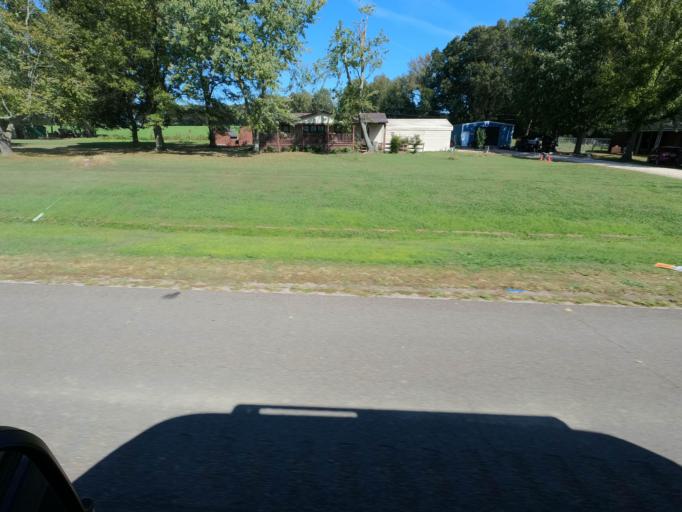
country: US
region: Tennessee
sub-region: Crockett County
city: Bells
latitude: 35.7039
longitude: -89.0337
